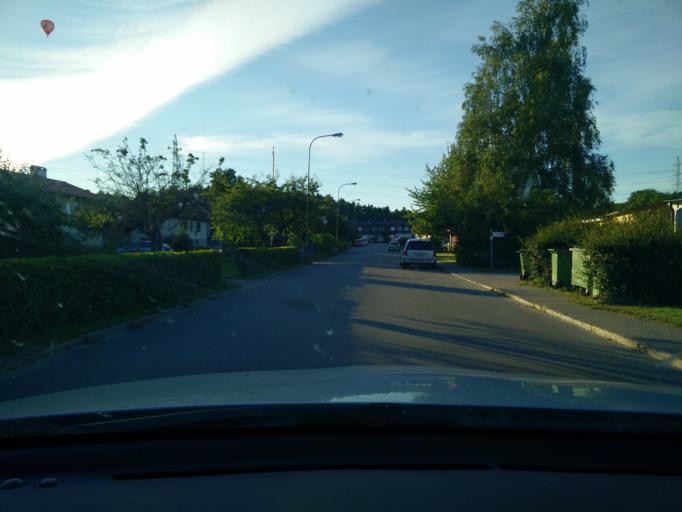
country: SE
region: Stockholm
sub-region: Sollentuna Kommun
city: Sollentuna
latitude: 59.4502
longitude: 17.9579
